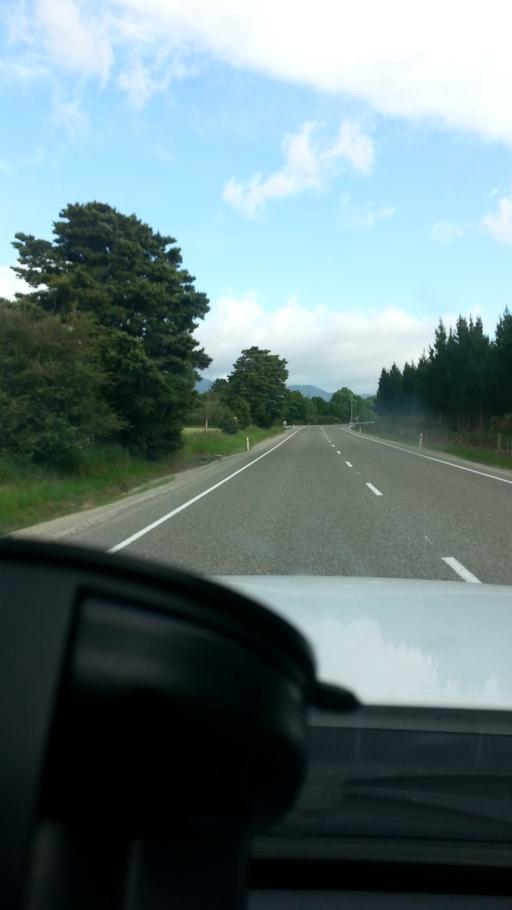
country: NZ
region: Wellington
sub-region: Masterton District
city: Masterton
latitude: -40.8112
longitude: 175.6214
